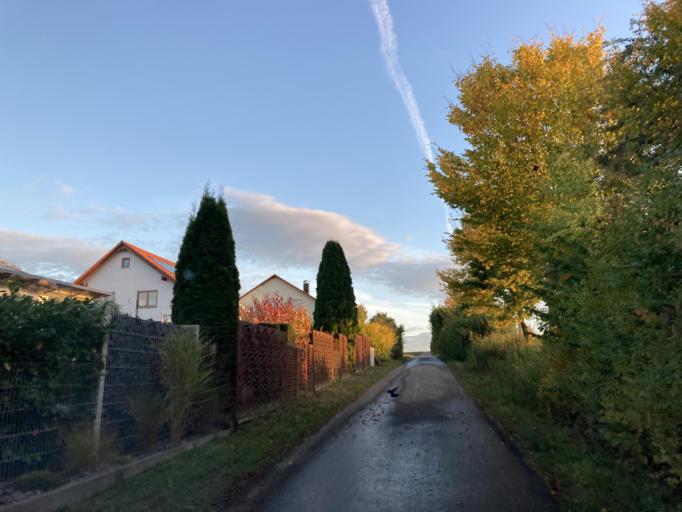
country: DE
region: Baden-Wuerttemberg
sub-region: Regierungsbezirk Stuttgart
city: Bondorf
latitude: 48.4889
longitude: 8.8001
